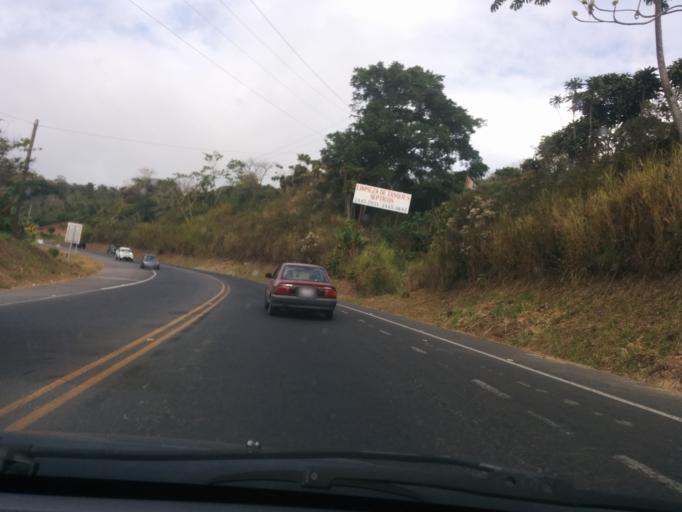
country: CR
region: Alajuela
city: San Rafael
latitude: 10.0625
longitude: -84.4478
